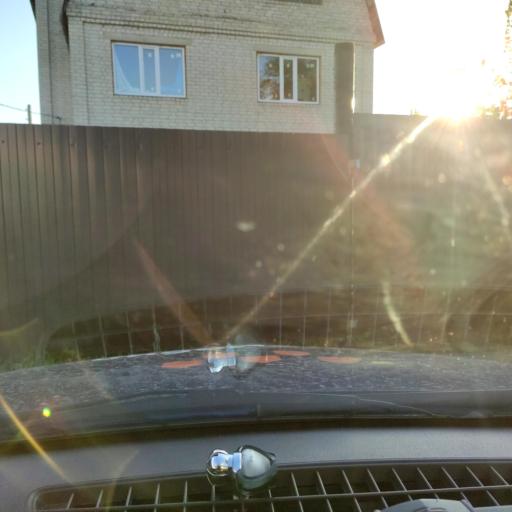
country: RU
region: Voronezj
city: Pridonskoy
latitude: 51.7086
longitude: 39.0711
